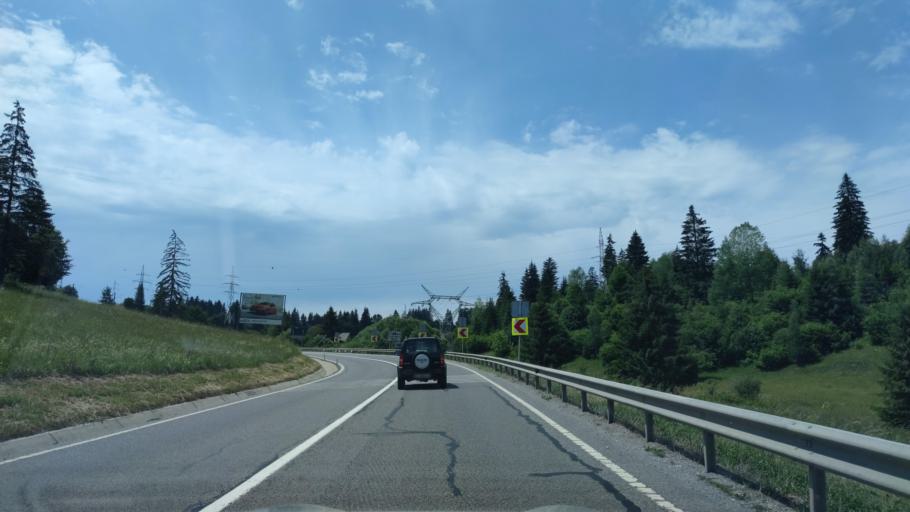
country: RO
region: Harghita
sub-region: Comuna Sandominic
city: Sandominic
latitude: 46.6256
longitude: 25.7271
